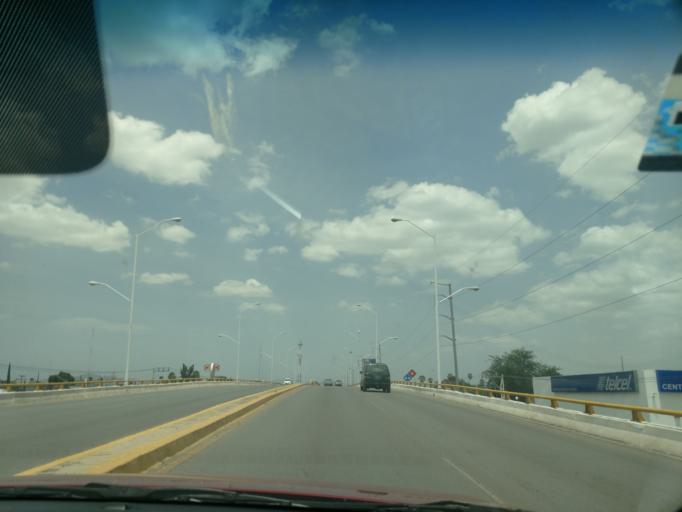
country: MX
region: San Luis Potosi
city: Rio Verde
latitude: 21.9233
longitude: -99.9952
